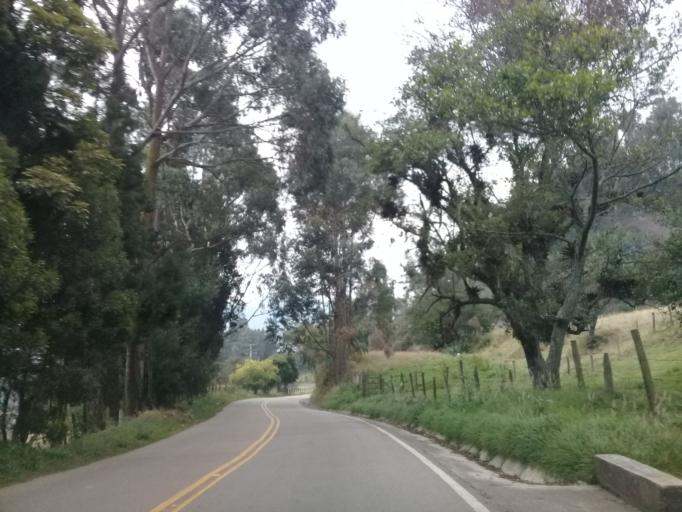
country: CO
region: Cundinamarca
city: Zipaquira
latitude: 5.0323
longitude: -74.0372
